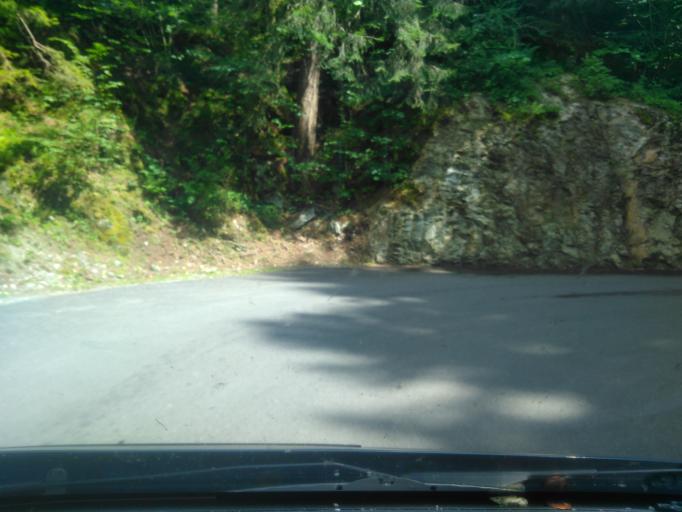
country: CH
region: Bern
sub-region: Interlaken-Oberhasli District
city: Meiringen
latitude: 46.6992
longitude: 8.2253
